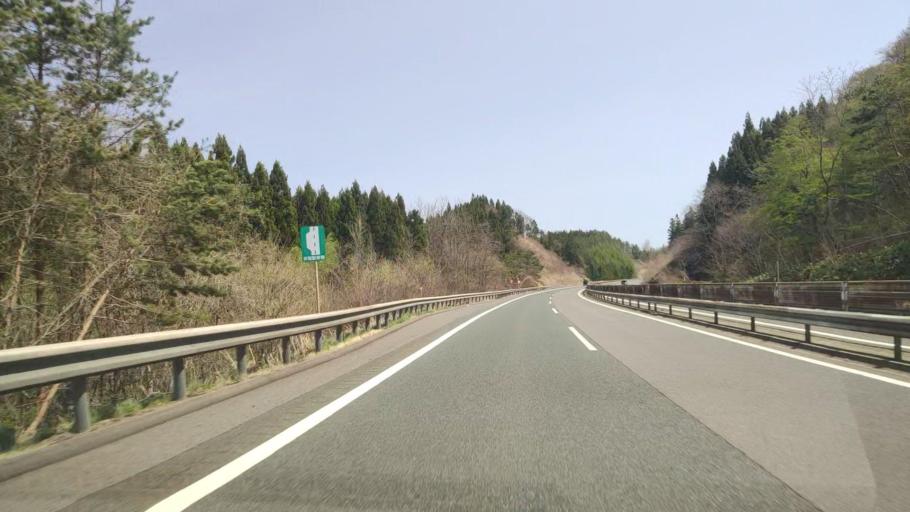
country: JP
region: Iwate
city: Ichinohe
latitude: 40.1149
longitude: 141.0761
